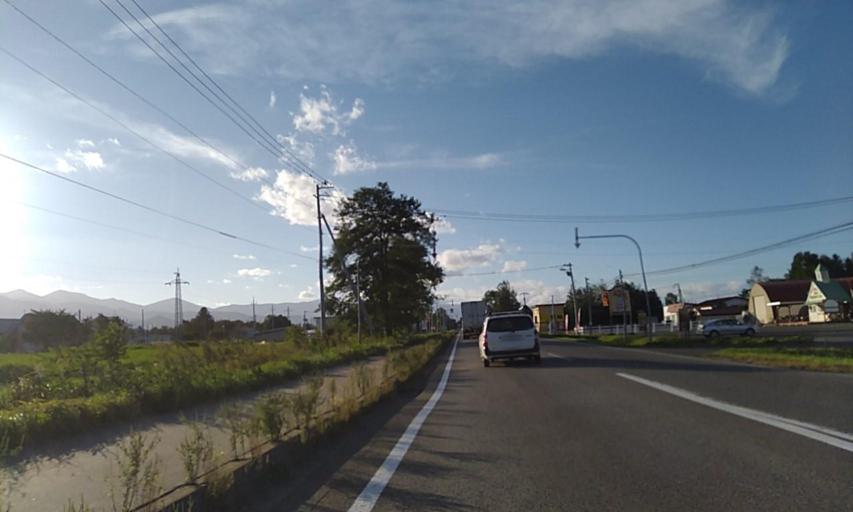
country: JP
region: Hokkaido
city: Otofuke
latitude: 42.9434
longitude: 142.9486
